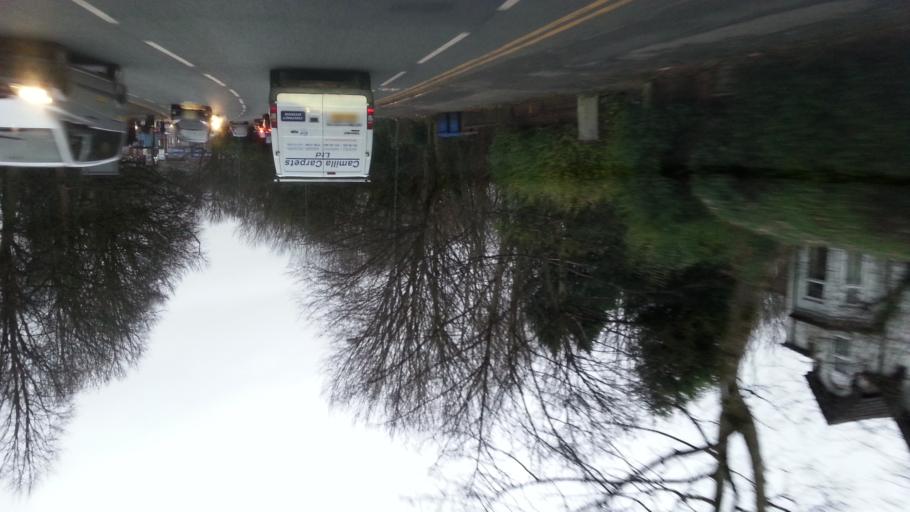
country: GB
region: England
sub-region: Borough of Bury
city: Prestwich
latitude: 53.5163
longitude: -2.2705
